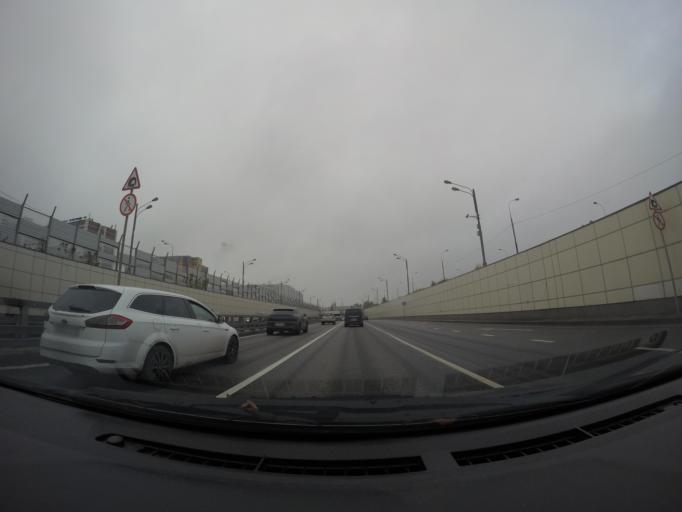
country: RU
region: Moscow
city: Shchukino
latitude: 55.7724
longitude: 37.4185
